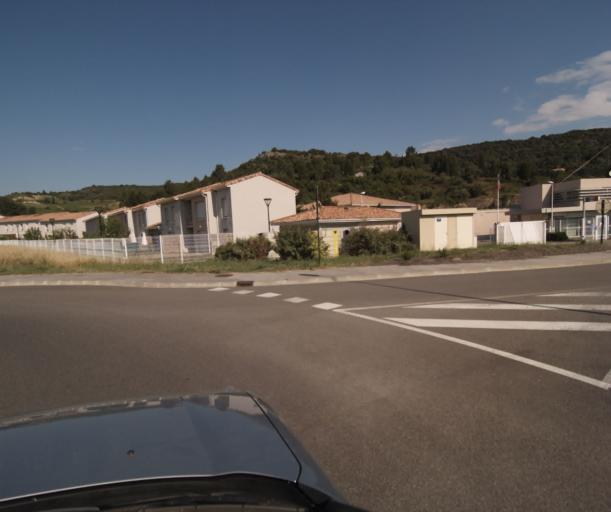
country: FR
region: Languedoc-Roussillon
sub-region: Departement de l'Aude
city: Limoux
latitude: 43.0741
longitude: 2.2172
